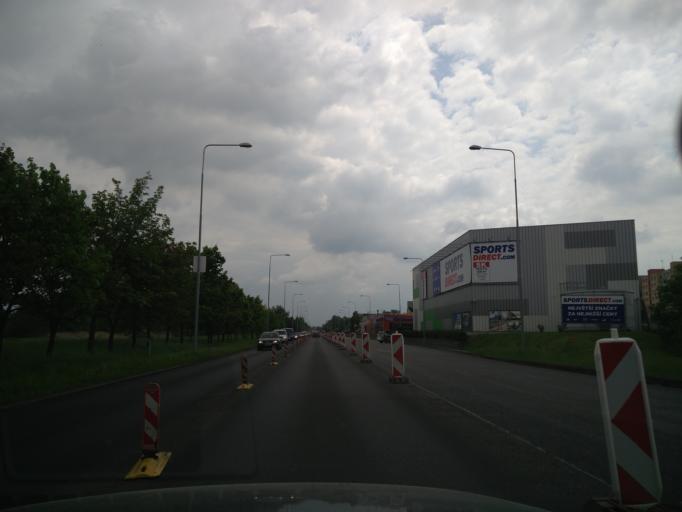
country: CZ
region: Jihocesky
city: Hrdejovice
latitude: 49.0009
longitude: 14.4540
